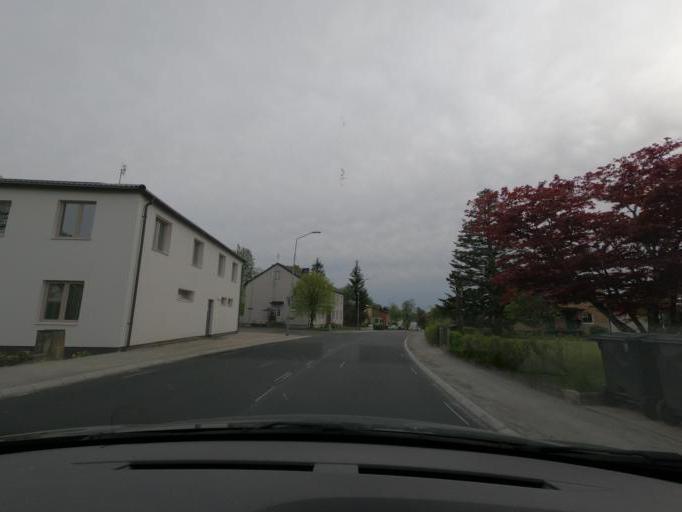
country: SE
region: Joenkoeping
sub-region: Varnamo Kommun
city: Bredaryd
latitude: 57.2207
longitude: 13.7832
